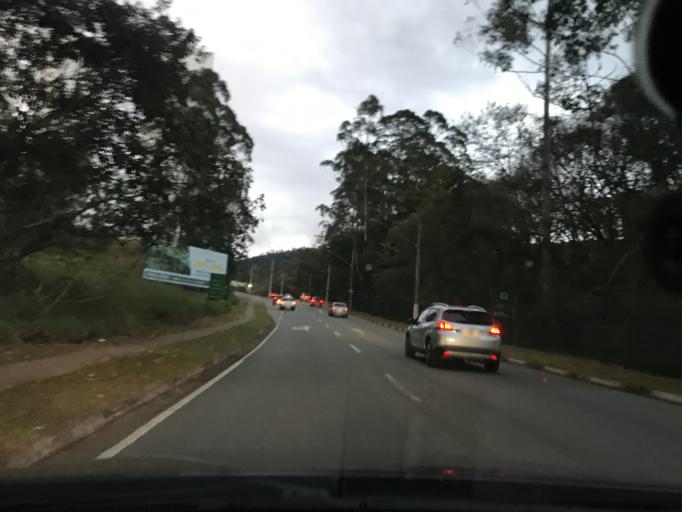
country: BR
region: Sao Paulo
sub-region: Barueri
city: Barueri
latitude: -23.4693
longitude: -46.8424
